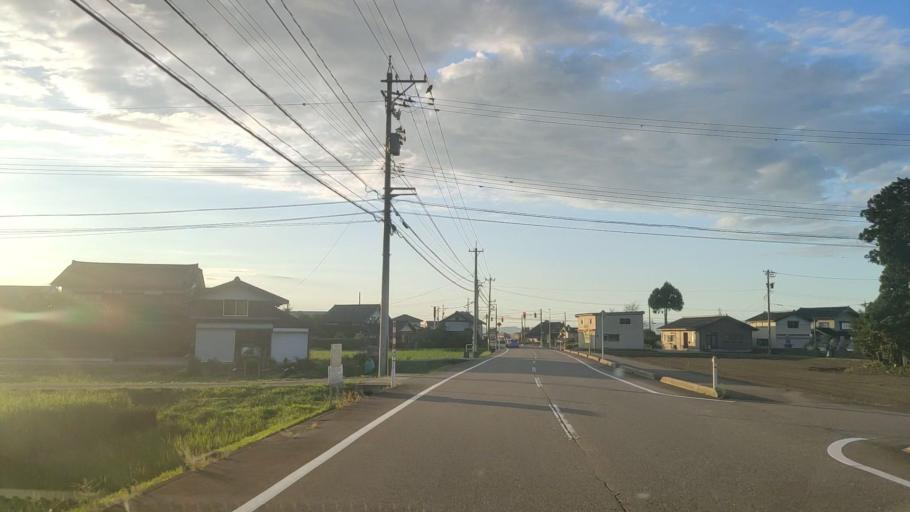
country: JP
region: Toyama
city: Nanto-shi
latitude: 36.5977
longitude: 136.9452
